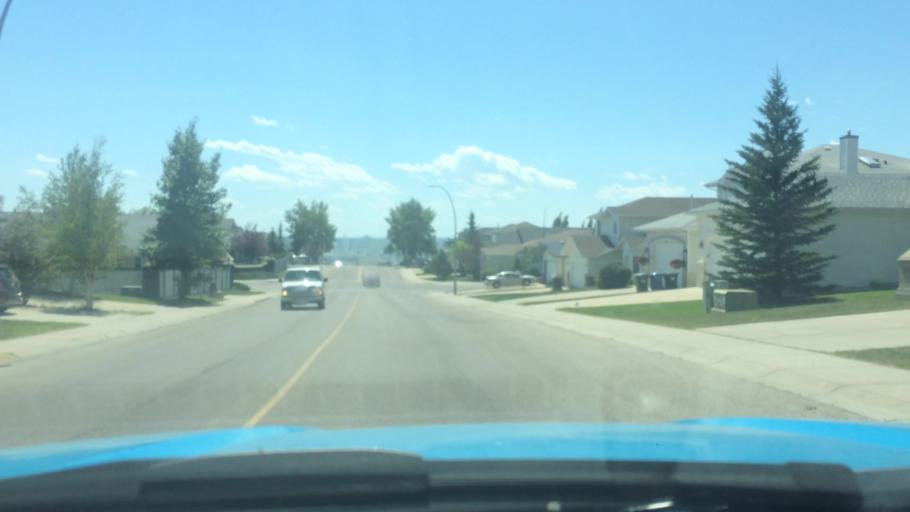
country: CA
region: Alberta
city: Calgary
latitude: 51.1361
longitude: -114.1915
